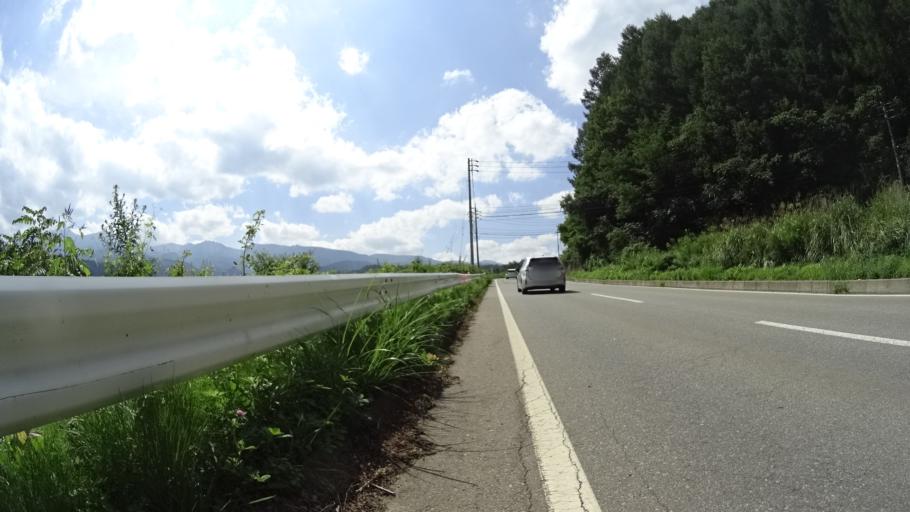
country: JP
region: Nagano
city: Saku
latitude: 36.0552
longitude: 138.4503
